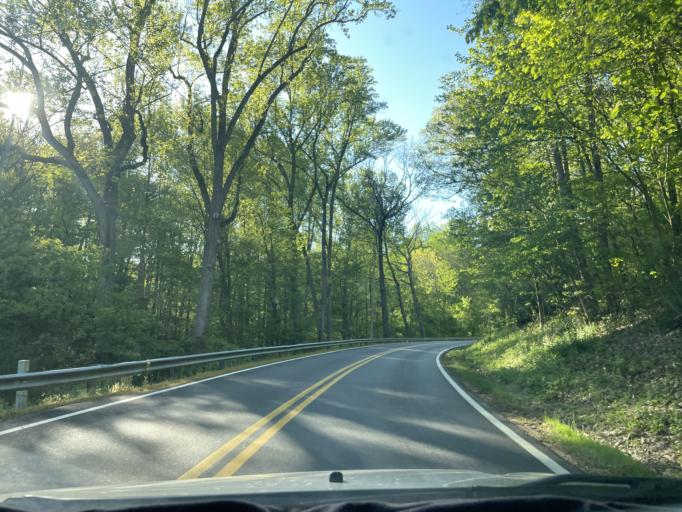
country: US
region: Maryland
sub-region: Carroll County
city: Mount Airy
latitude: 39.4179
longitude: -77.1396
